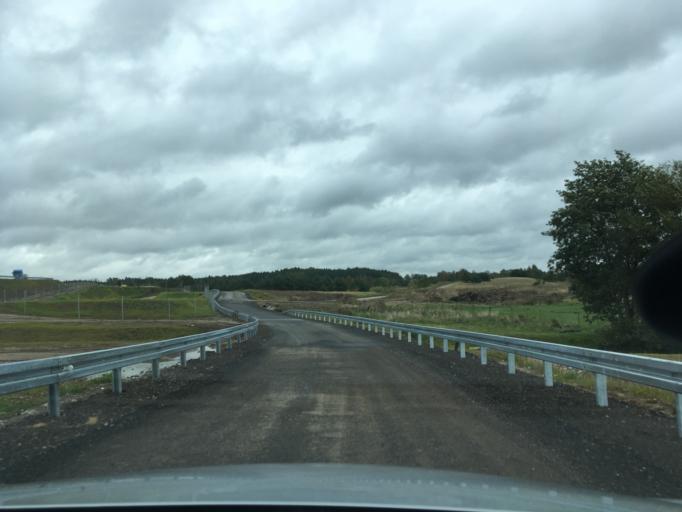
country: PL
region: Pomeranian Voivodeship
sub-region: Powiat koscierski
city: Koscierzyna
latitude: 54.1113
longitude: 18.0015
